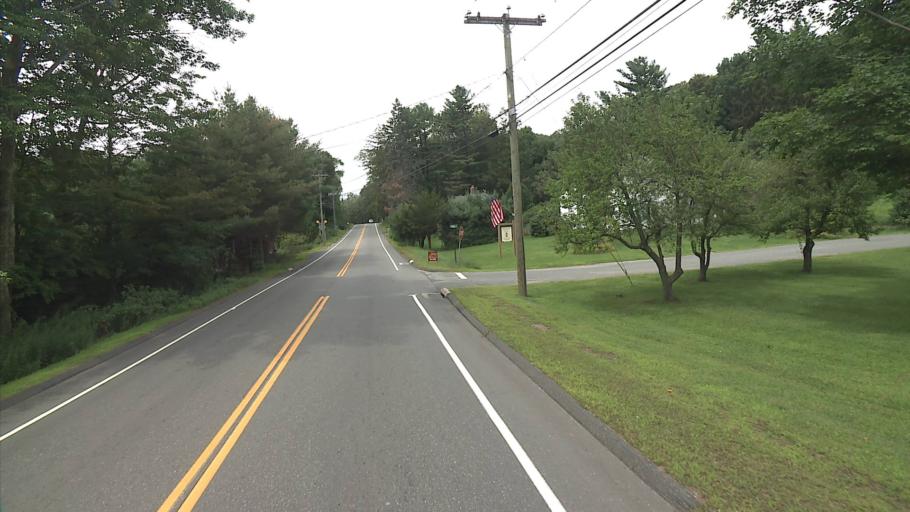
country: US
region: Connecticut
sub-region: Tolland County
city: Storrs
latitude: 41.8759
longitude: -72.2651
